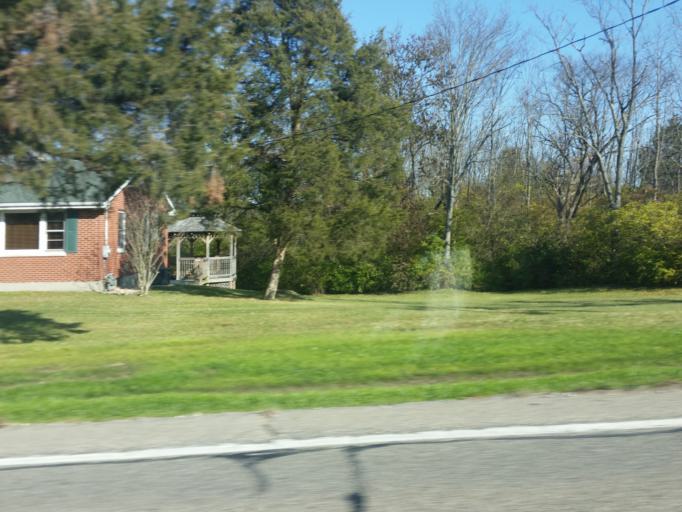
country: US
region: Ohio
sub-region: Butler County
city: Oxford
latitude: 39.4835
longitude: -84.7159
